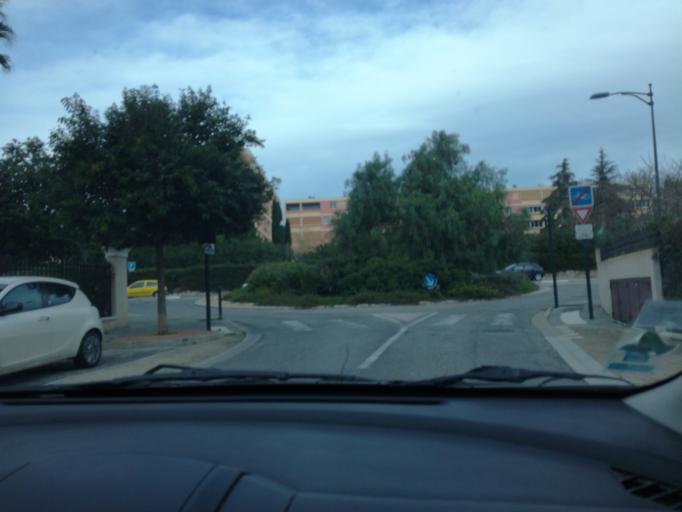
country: FR
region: Provence-Alpes-Cote d'Azur
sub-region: Departement du Var
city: Hyeres
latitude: 43.1216
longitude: 6.1161
